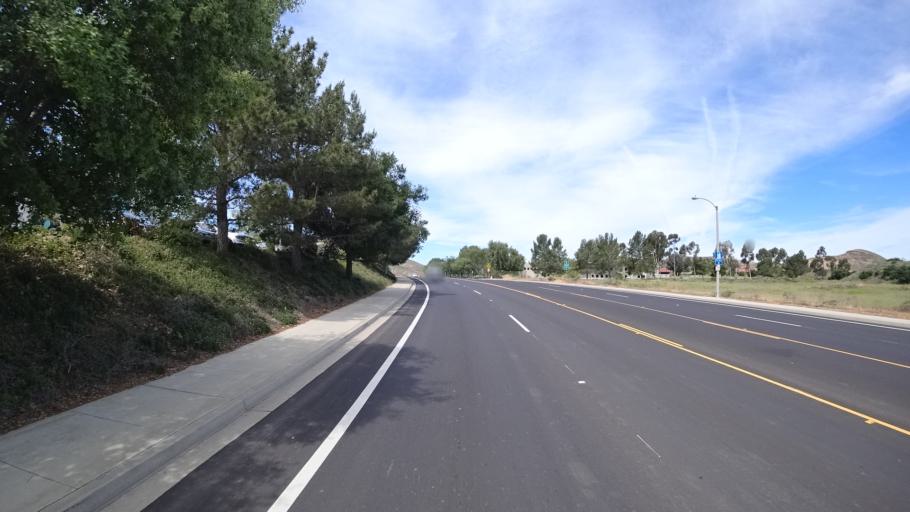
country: US
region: California
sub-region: Ventura County
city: Casa Conejo
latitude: 34.2044
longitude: -118.9269
